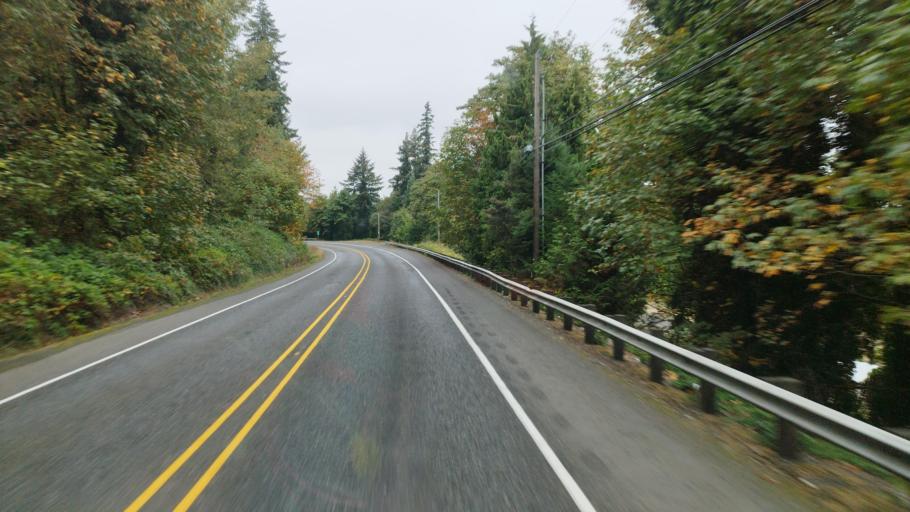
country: US
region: Oregon
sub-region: Columbia County
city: Rainier
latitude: 46.0820
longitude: -122.9136
